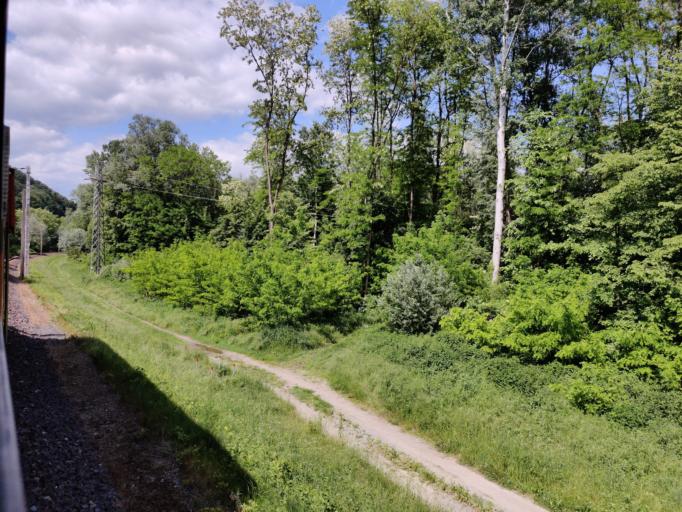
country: AT
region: Styria
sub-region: Politischer Bezirk Leibnitz
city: Stocking
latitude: 46.8631
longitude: 15.5304
